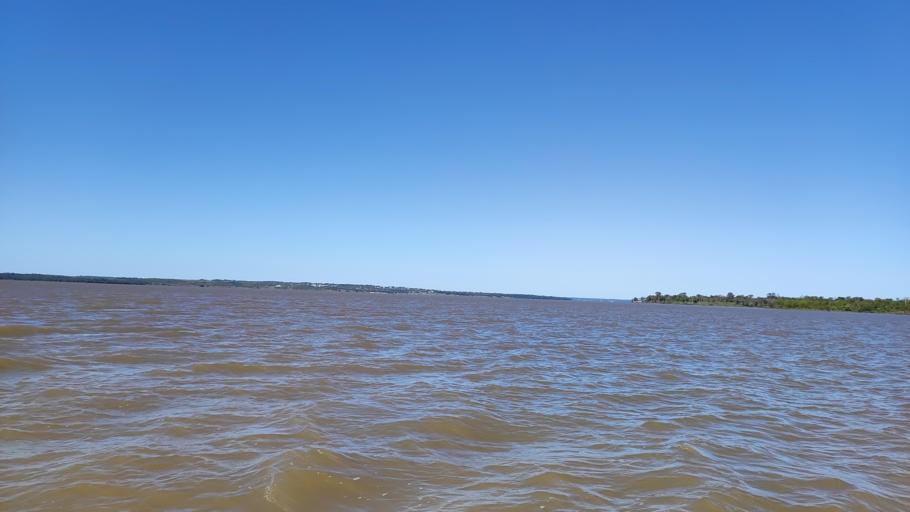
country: PY
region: Itapua
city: San Juan del Parana
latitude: -27.3466
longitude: -56.0364
